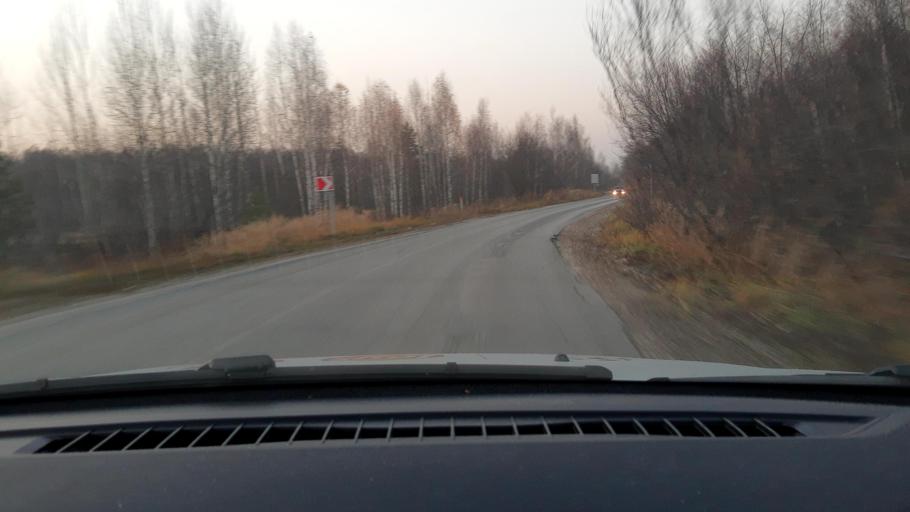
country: RU
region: Nizjnij Novgorod
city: Neklyudovo
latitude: 56.4279
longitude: 43.9241
